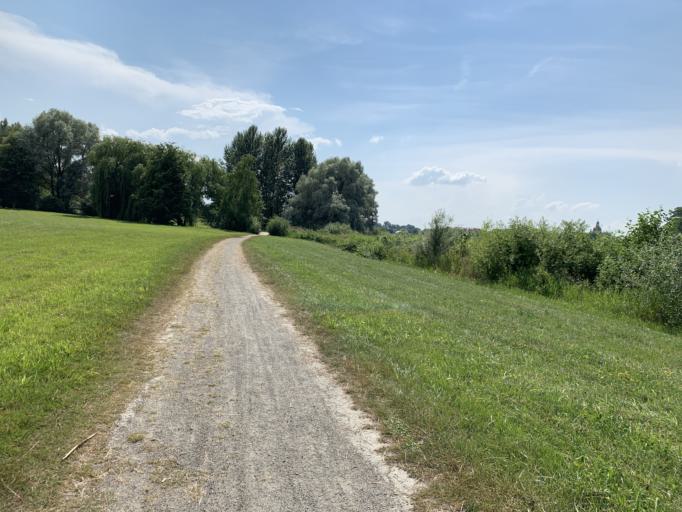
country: BY
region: Minsk
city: Nyasvizh
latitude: 53.2214
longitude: 26.6967
